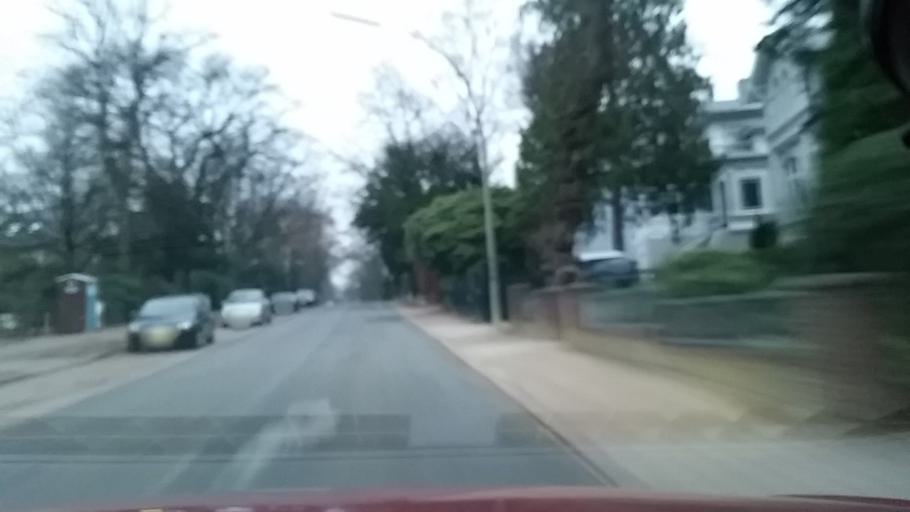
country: DE
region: Schleswig-Holstein
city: Halstenbek
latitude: 53.5656
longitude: 9.8116
